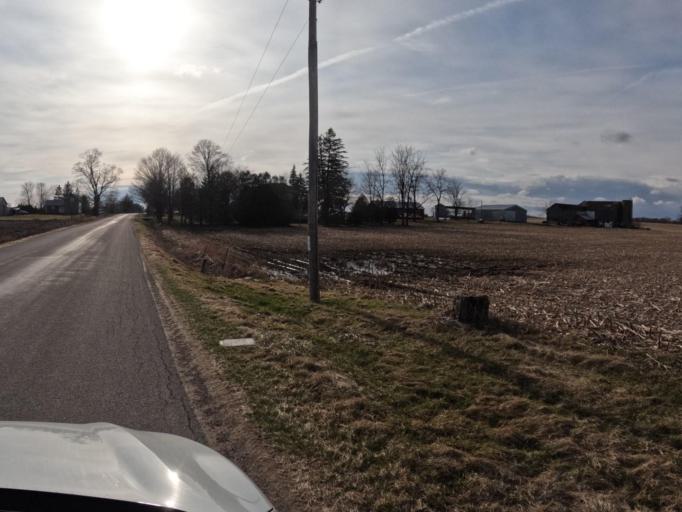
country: CA
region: Ontario
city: Brant
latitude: 42.9975
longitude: -80.4624
